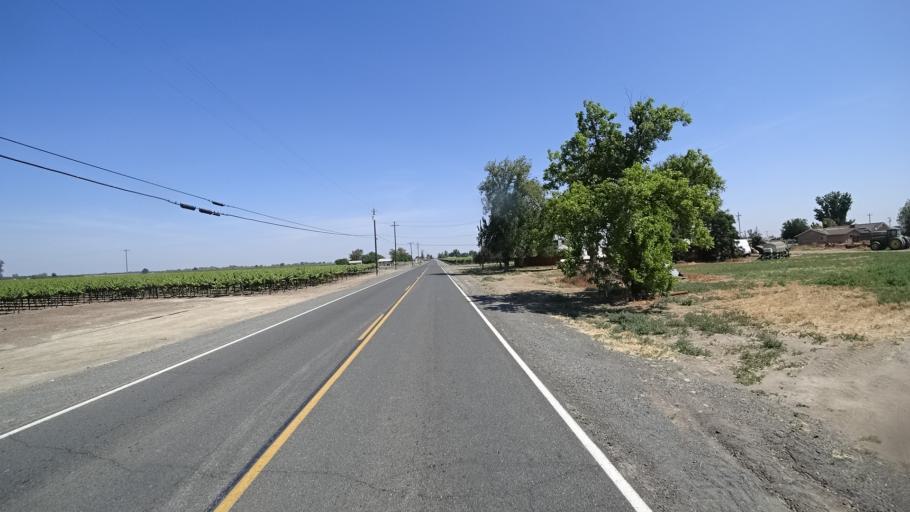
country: US
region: California
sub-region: Fresno County
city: Riverdale
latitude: 36.3647
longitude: -119.8513
